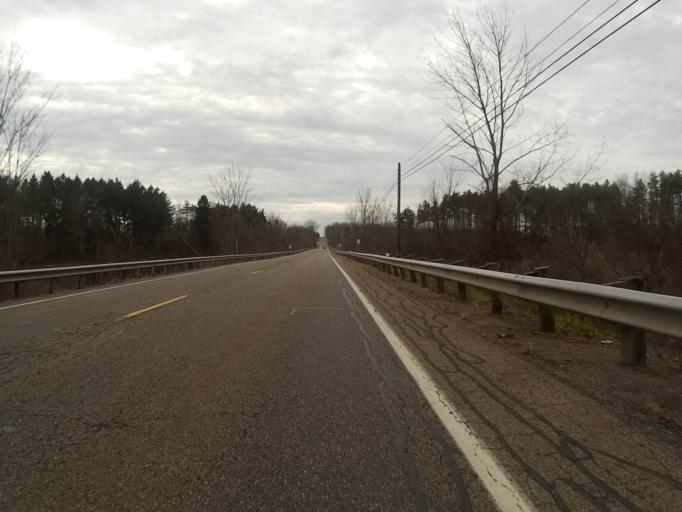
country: US
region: Ohio
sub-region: Portage County
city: Brimfield
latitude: 41.0542
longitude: -81.3473
